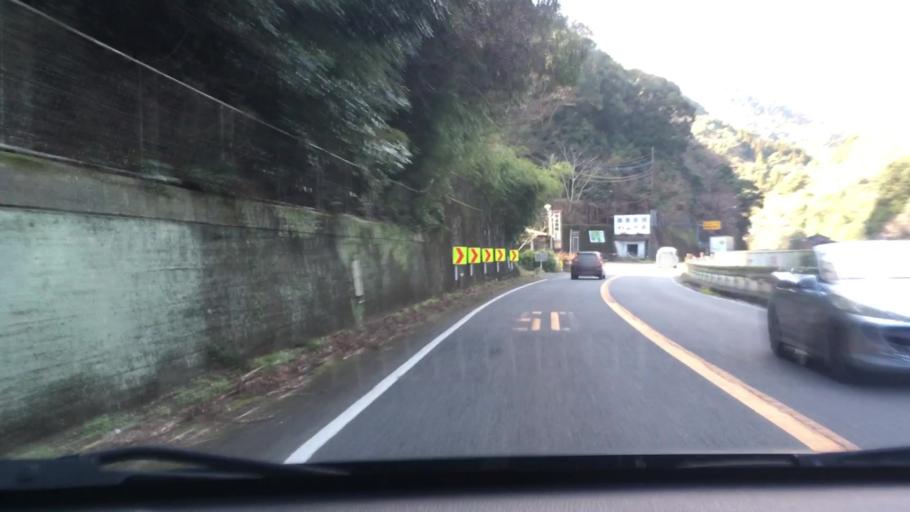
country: JP
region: Oita
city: Tsukumiura
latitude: 33.0033
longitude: 131.7994
